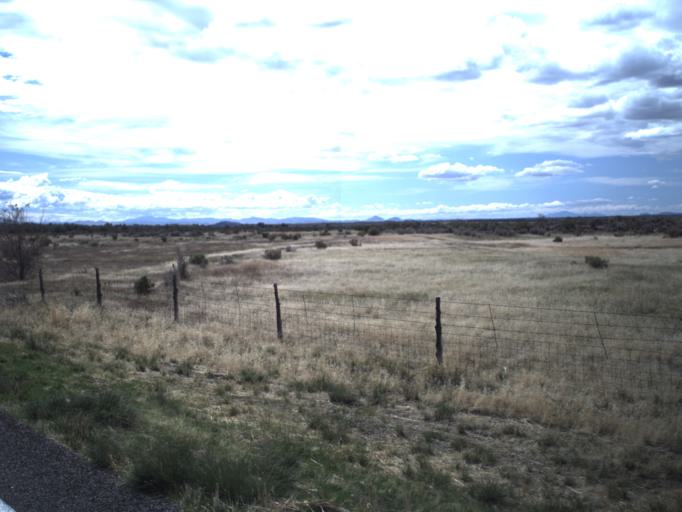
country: US
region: Utah
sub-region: Millard County
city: Fillmore
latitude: 39.0959
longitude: -112.4100
